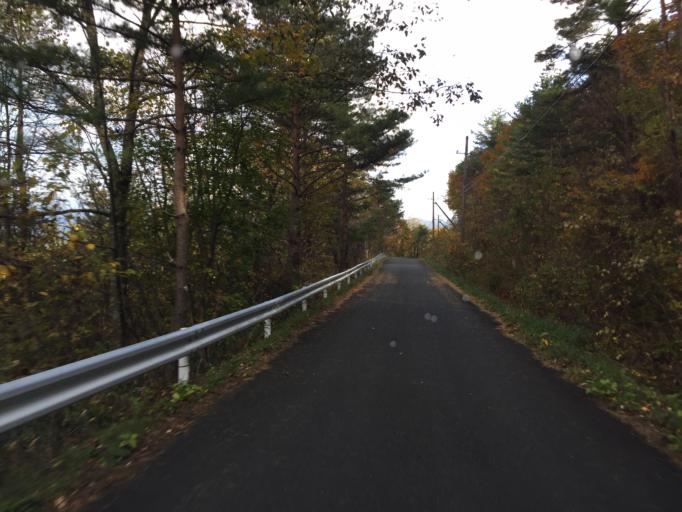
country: JP
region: Fukushima
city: Fukushima-shi
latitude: 37.7190
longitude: 140.3111
